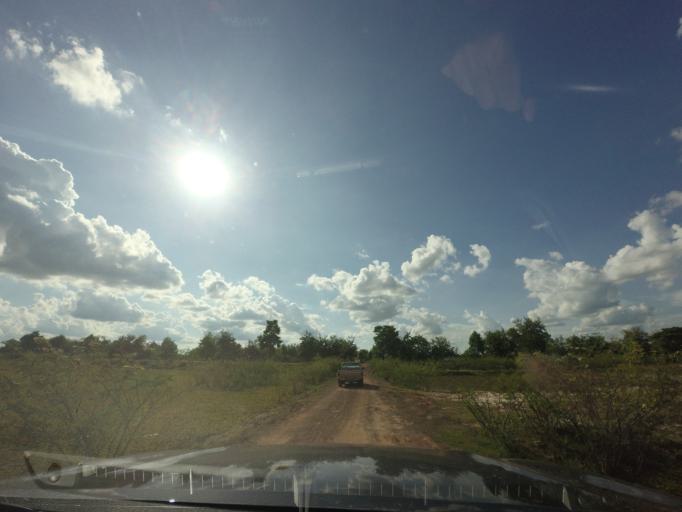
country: TH
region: Changwat Udon Thani
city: Ban Dung
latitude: 17.7453
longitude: 103.3577
